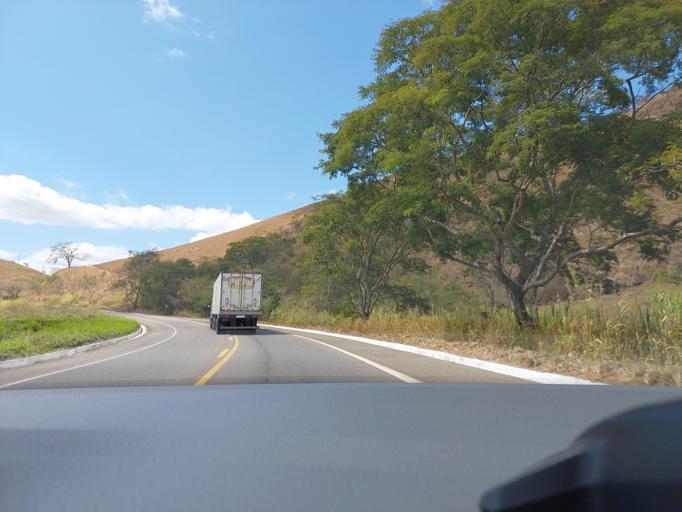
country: BR
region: Minas Gerais
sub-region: Muriae
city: Muriae
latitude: -21.1264
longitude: -42.2342
